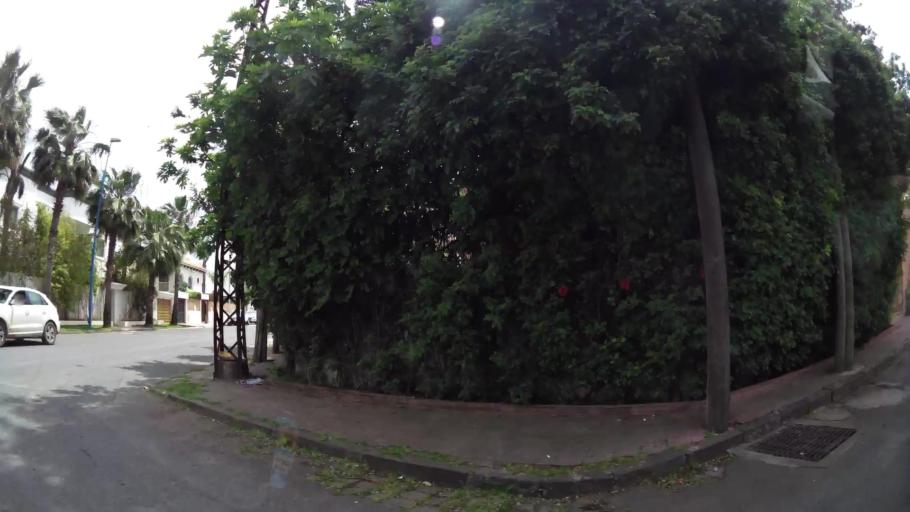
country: MA
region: Grand Casablanca
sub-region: Casablanca
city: Casablanca
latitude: 33.5574
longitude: -7.6434
